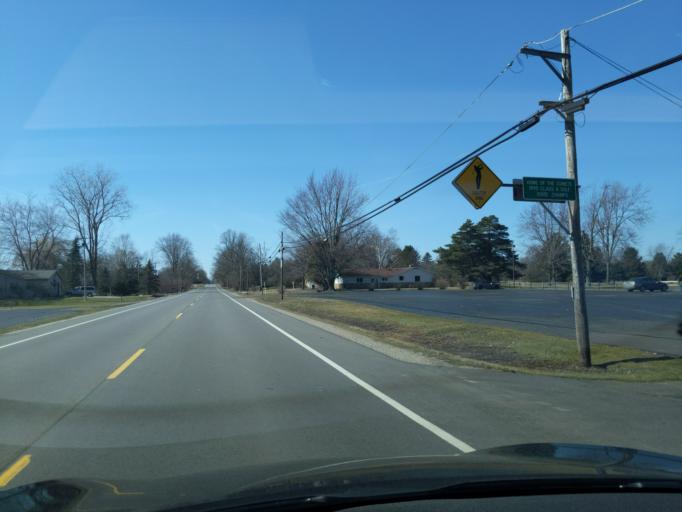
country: US
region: Michigan
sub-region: Eaton County
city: Grand Ledge
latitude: 42.7264
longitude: -84.7237
